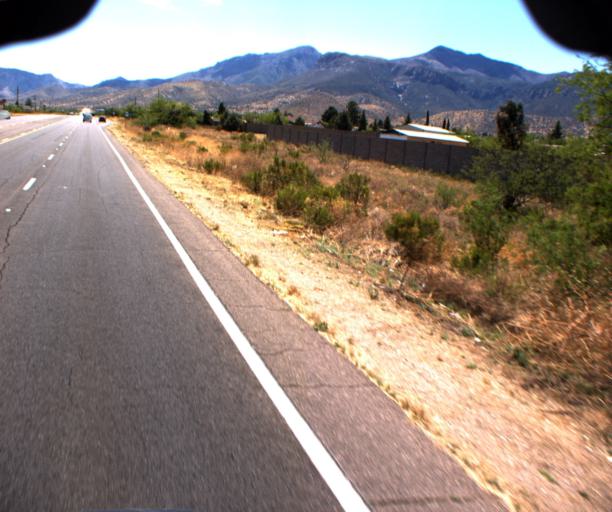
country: US
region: Arizona
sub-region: Cochise County
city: Sierra Vista Southeast
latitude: 31.4799
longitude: -110.2575
